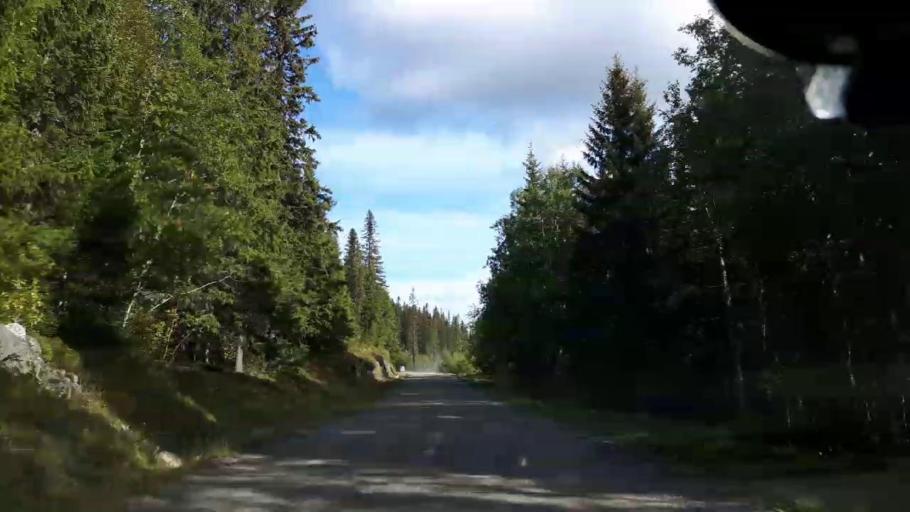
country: SE
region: Jaemtland
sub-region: Ragunda Kommun
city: Hammarstrand
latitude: 63.4116
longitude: 16.0885
